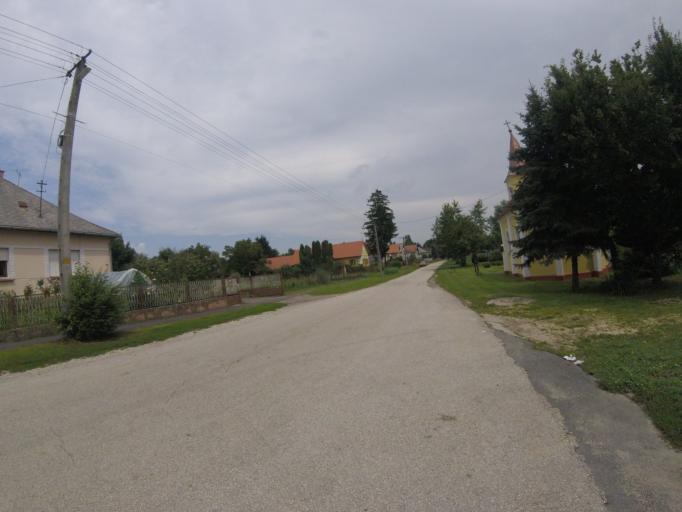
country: HR
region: Medimurska
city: Podturen
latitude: 46.5004
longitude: 16.5792
